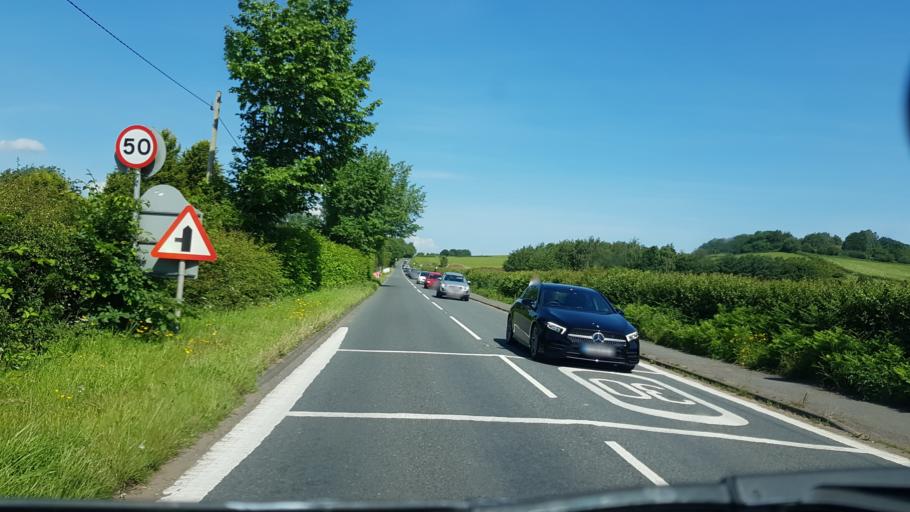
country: GB
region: England
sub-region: Worcestershire
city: Stourport-on-Severn
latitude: 52.3552
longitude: -2.2951
